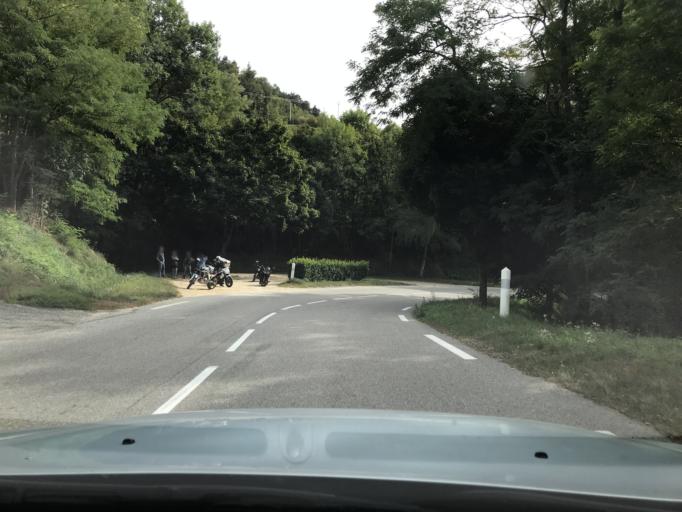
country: FR
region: Rhone-Alpes
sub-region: Departement de l'Ardeche
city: Lamastre
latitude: 44.9839
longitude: 4.5981
